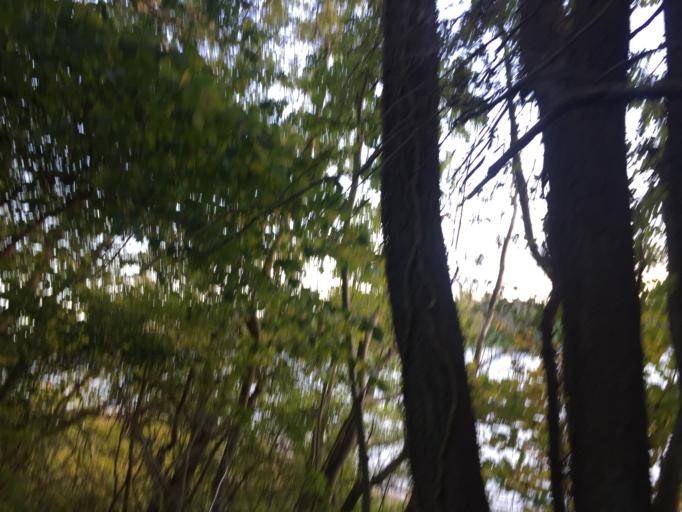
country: DK
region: Zealand
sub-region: Ringsted Kommune
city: Ringsted
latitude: 55.4835
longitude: 11.8155
